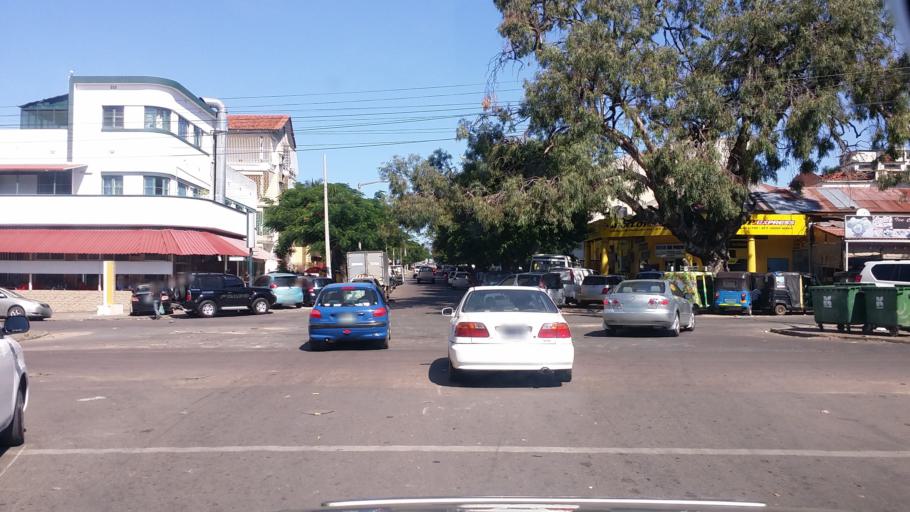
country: MZ
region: Maputo City
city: Maputo
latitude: -25.9603
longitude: 32.5778
